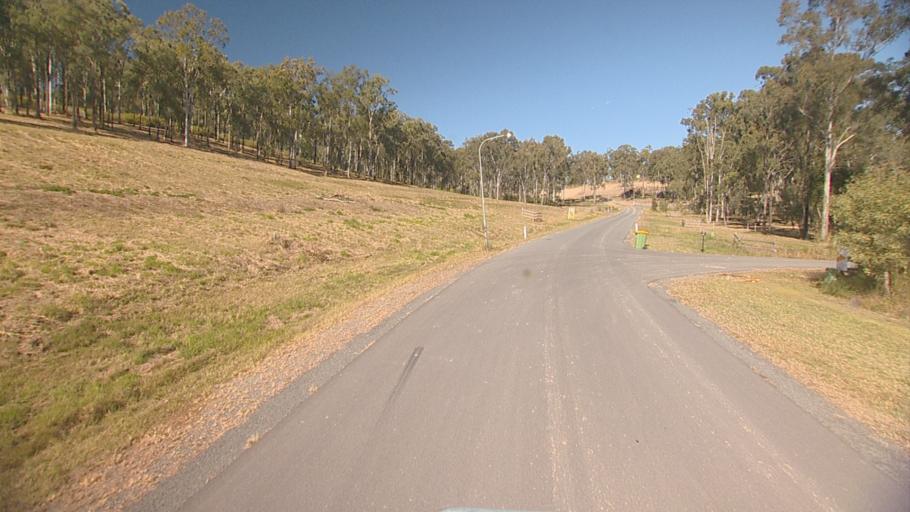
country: AU
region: Queensland
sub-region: Logan
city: Windaroo
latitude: -27.7729
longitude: 153.1460
